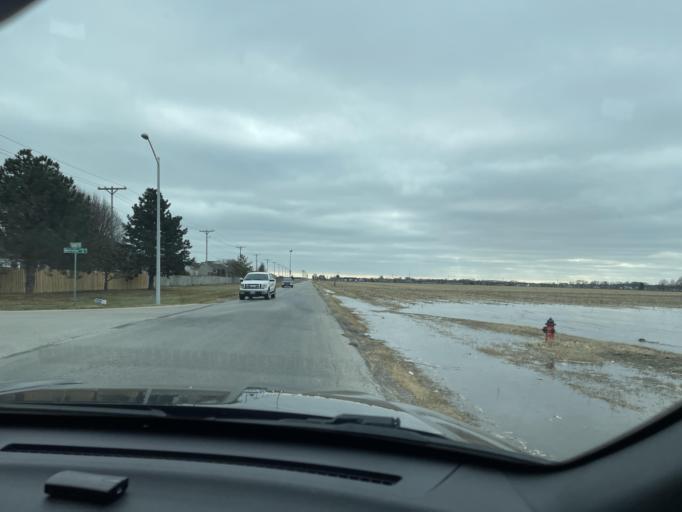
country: US
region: Illinois
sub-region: Sangamon County
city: Jerome
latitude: 39.7759
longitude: -89.7535
